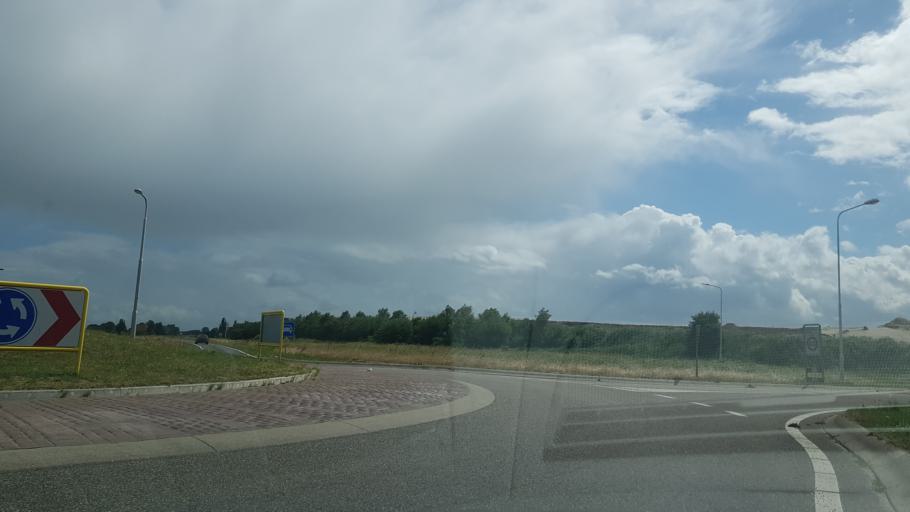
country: NL
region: Friesland
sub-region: Gemeente Ferwerderadiel
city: Burdaard
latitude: 53.2817
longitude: 5.9055
